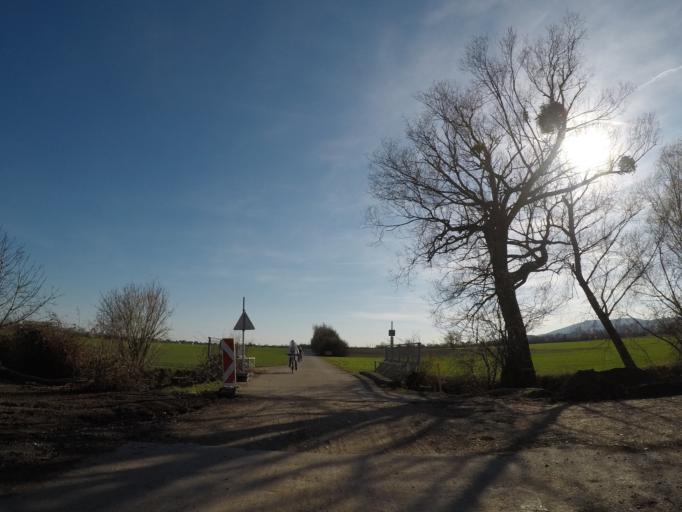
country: AT
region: Lower Austria
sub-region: Politischer Bezirk Modling
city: Biedermannsdorf
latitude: 48.0961
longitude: 16.3395
